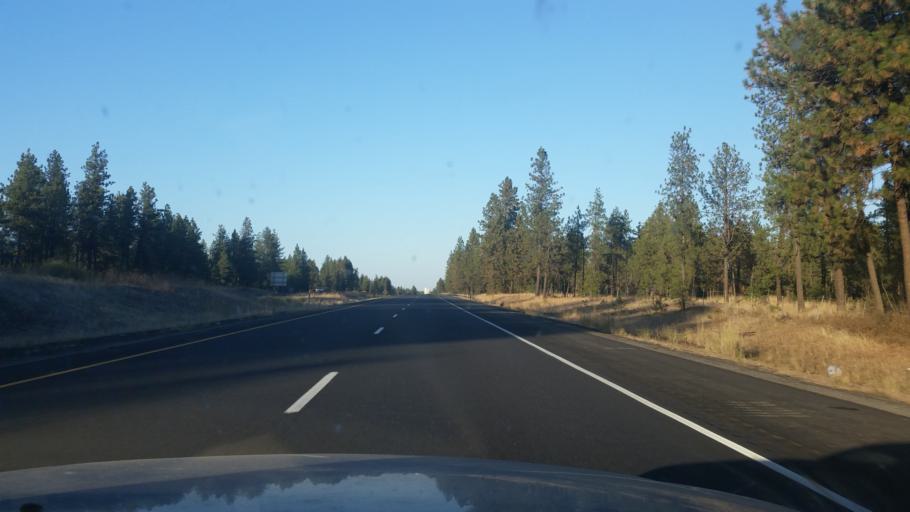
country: US
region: Washington
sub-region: Spokane County
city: Medical Lake
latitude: 47.5153
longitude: -117.6745
